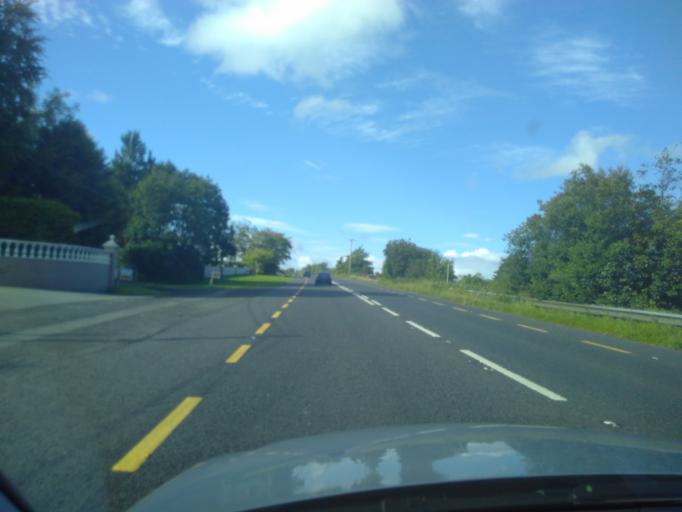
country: IE
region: Ulster
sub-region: County Donegal
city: Ballybofey
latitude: 54.8502
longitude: -7.7505
